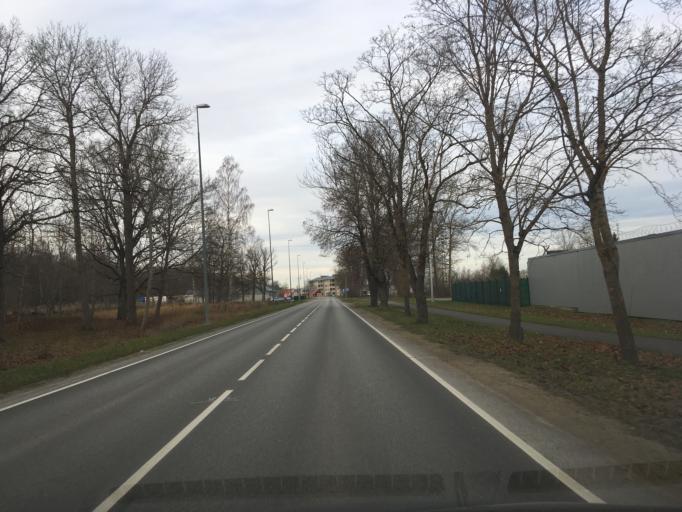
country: EE
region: Ida-Virumaa
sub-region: Johvi vald
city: Johvi
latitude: 59.3499
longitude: 27.4334
